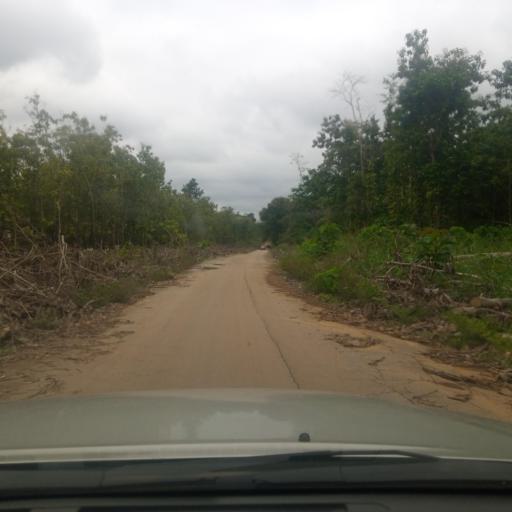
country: NG
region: Ebonyi
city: Effium
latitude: 6.6202
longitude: 8.0445
